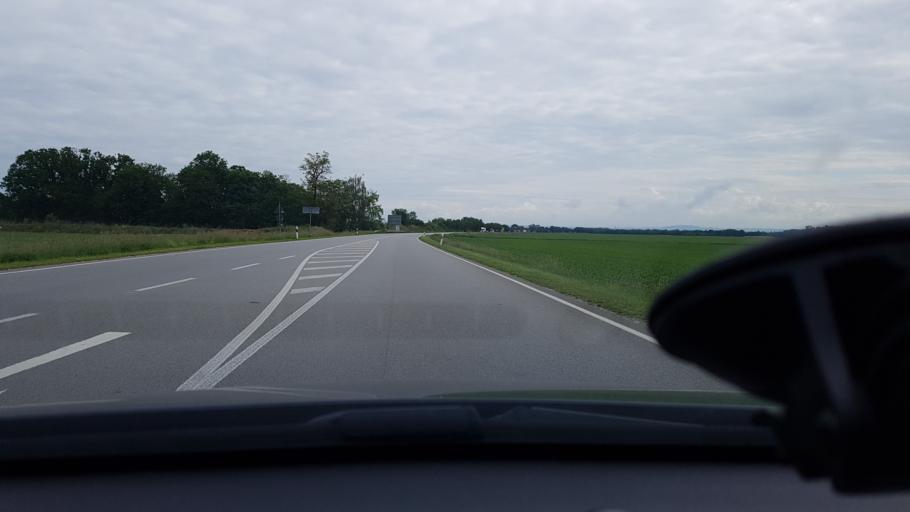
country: DE
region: Bavaria
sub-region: Lower Bavaria
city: Kirchham
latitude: 48.3693
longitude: 13.2775
